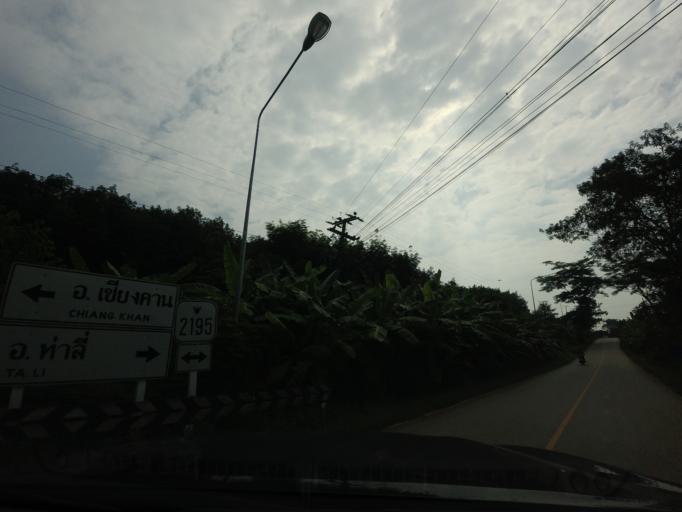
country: TH
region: Loei
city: Chiang Khan
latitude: 17.8105
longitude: 101.5610
